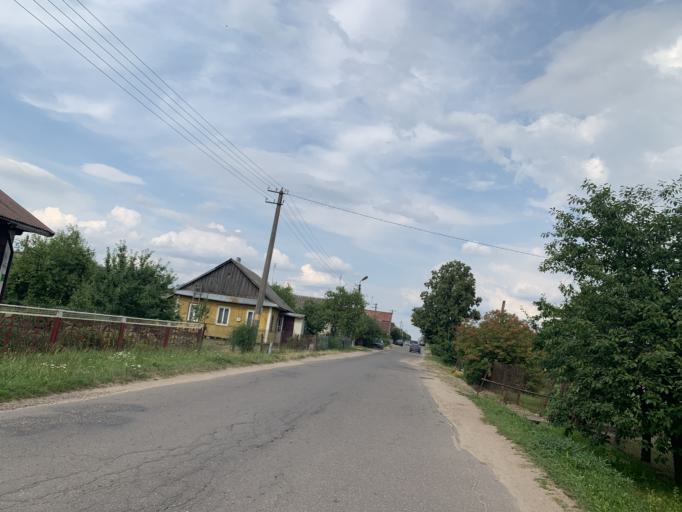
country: BY
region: Minsk
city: Nyasvizh
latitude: 53.2064
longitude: 26.6836
